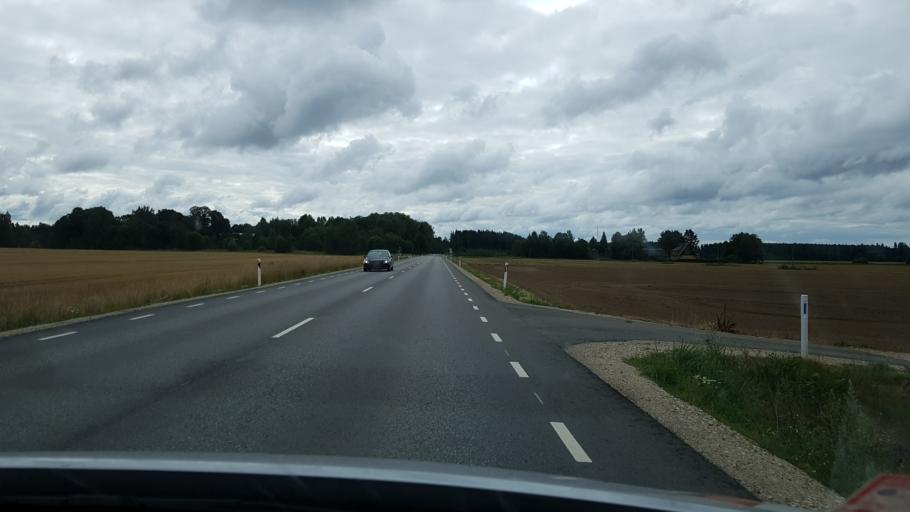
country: EE
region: Polvamaa
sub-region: Polva linn
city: Polva
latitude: 58.0287
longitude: 27.1533
